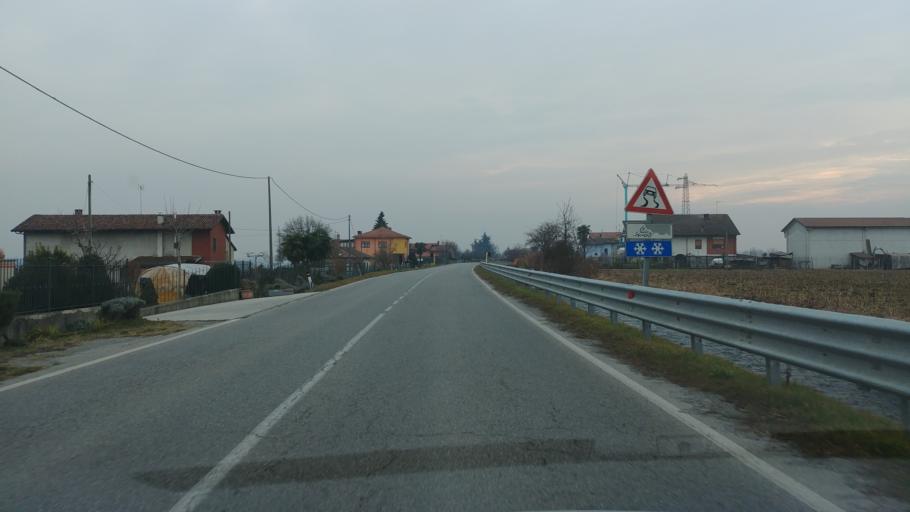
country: IT
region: Piedmont
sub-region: Provincia di Cuneo
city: Sant'Albano Stura
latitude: 44.5251
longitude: 7.7043
